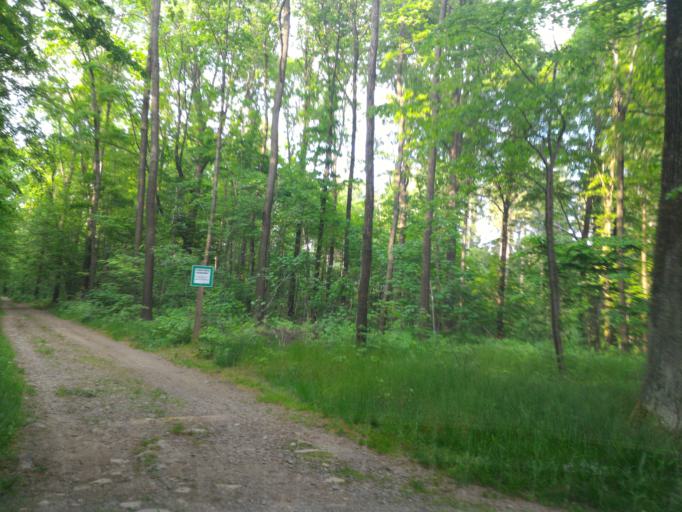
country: DE
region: Saxony
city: Grossschonau
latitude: 50.8716
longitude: 14.6643
